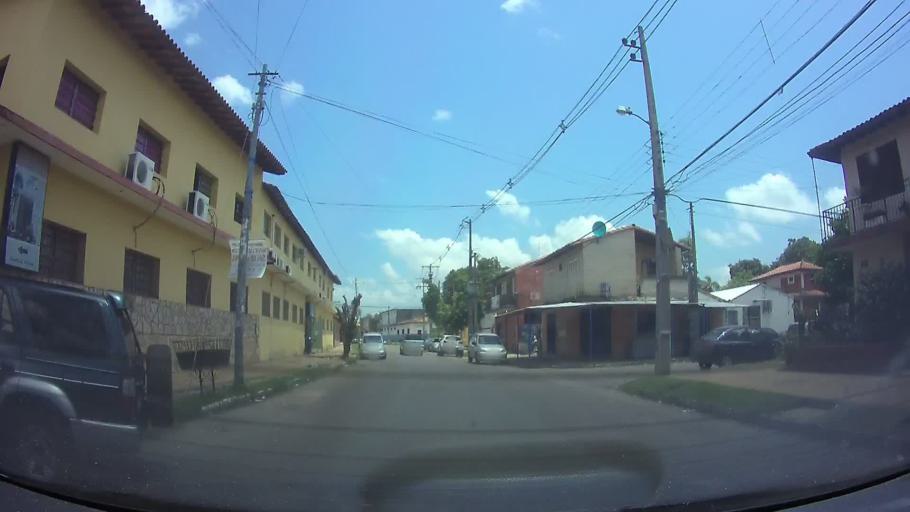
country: PY
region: Central
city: Fernando de la Mora
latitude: -25.2989
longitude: -57.5488
